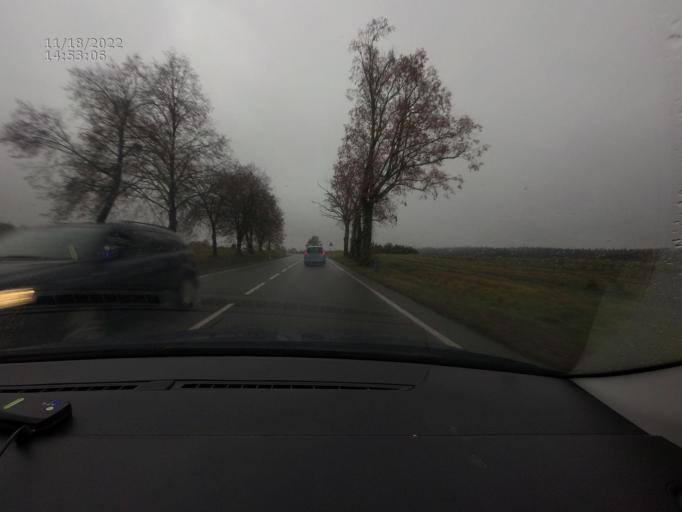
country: CZ
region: Jihocesky
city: Milevsko
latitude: 49.4551
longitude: 14.3465
